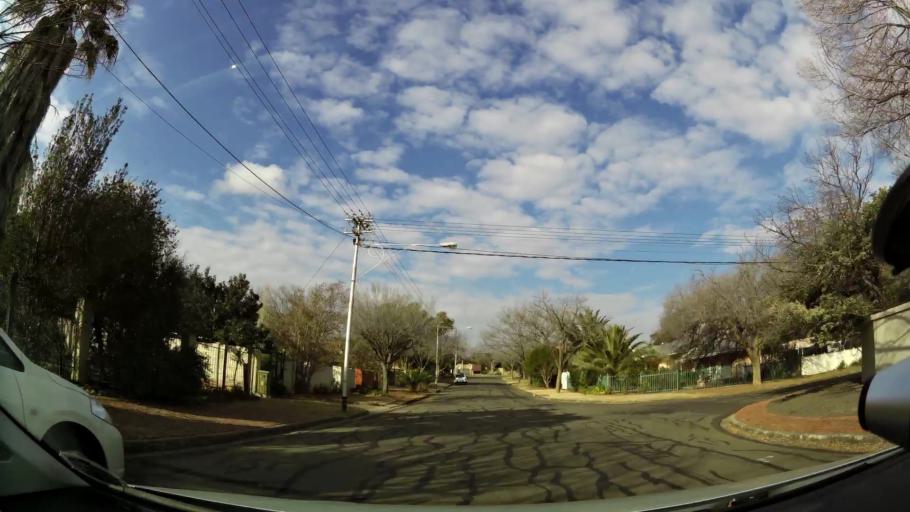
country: ZA
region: Orange Free State
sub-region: Mangaung Metropolitan Municipality
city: Bloemfontein
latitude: -29.0789
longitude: 26.2170
